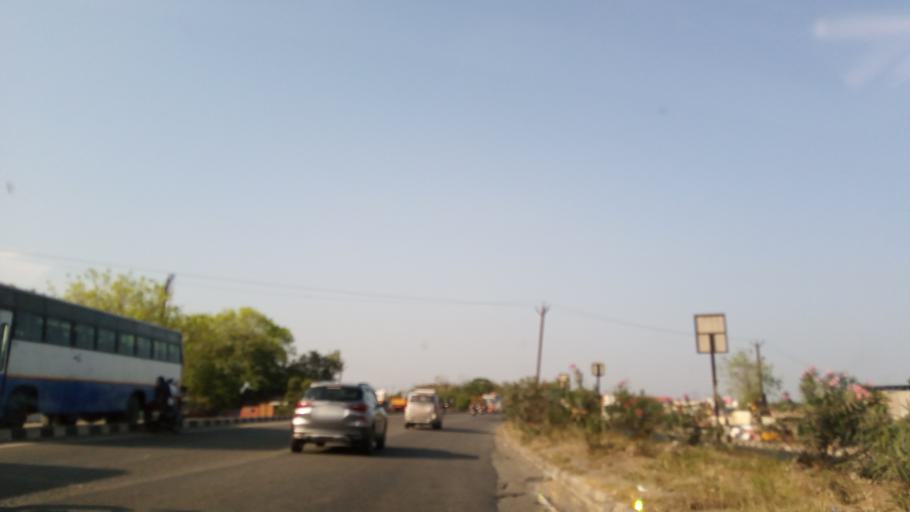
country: IN
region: Tamil Nadu
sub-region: Kancheepuram
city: Poonamalle
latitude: 13.0535
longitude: 80.0905
